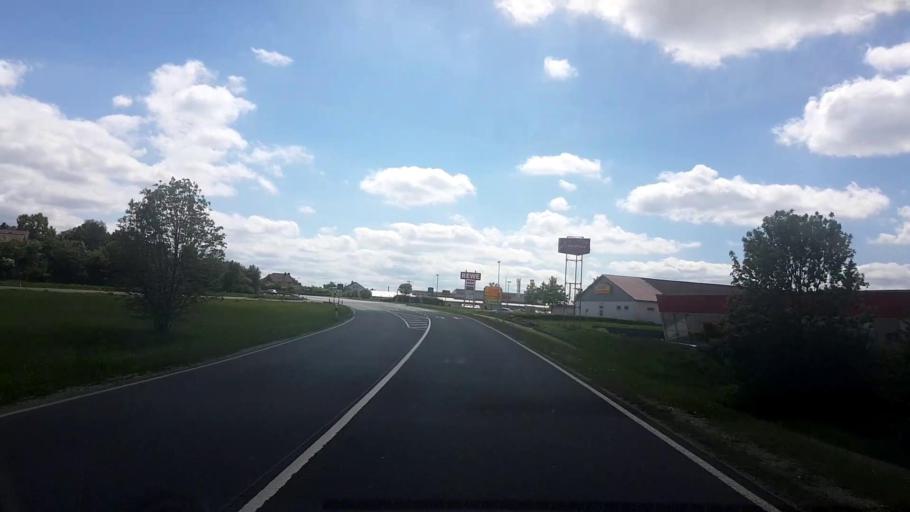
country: DE
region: Bavaria
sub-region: Upper Franconia
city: Untersiemau
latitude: 50.1985
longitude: 10.9668
